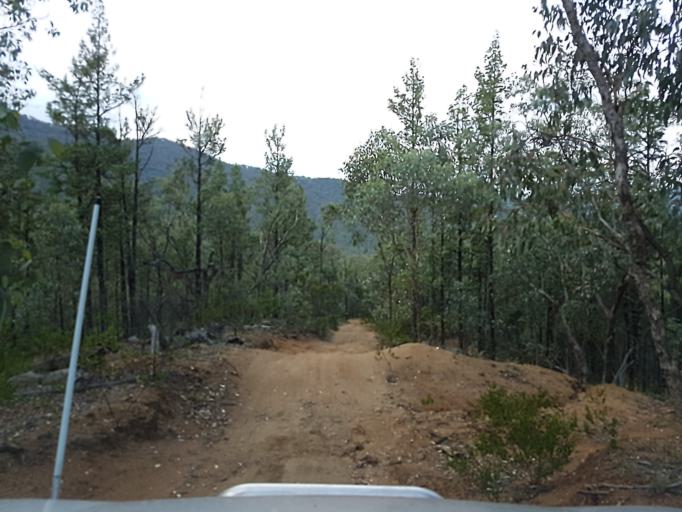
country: AU
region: New South Wales
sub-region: Snowy River
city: Jindabyne
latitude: -36.9510
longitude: 148.3802
